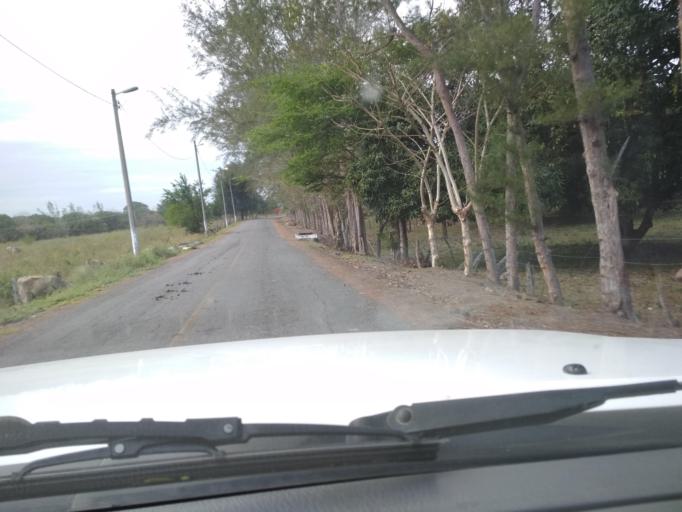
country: MX
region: Veracruz
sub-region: Veracruz
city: Delfino Victoria (Santa Fe)
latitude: 19.1566
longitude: -96.2934
